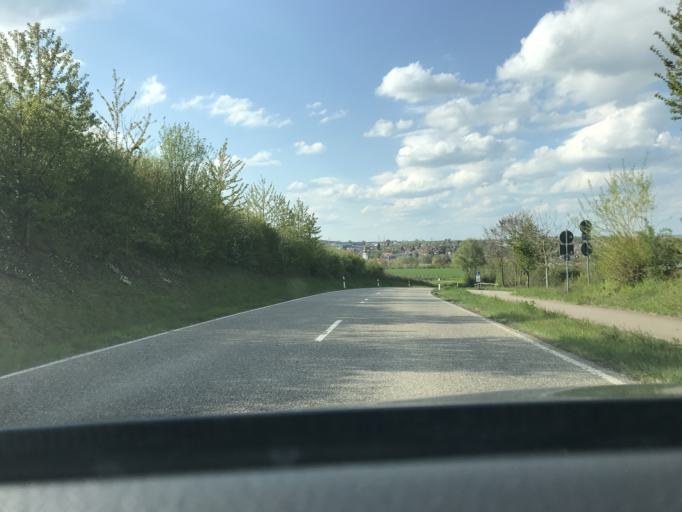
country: DE
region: Baden-Wuerttemberg
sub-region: Regierungsbezirk Stuttgart
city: Nordheim
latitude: 49.0994
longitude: 9.1360
